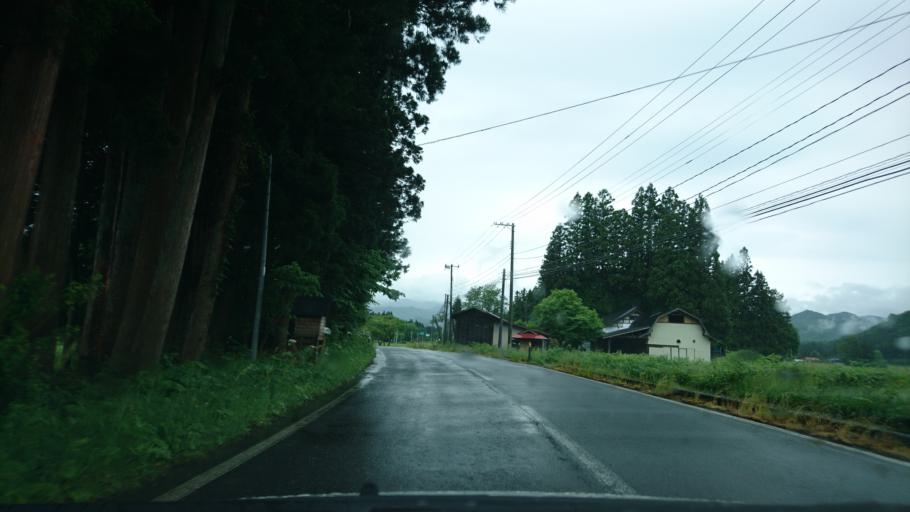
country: JP
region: Iwate
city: Ichinoseki
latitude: 38.9729
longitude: 140.9665
